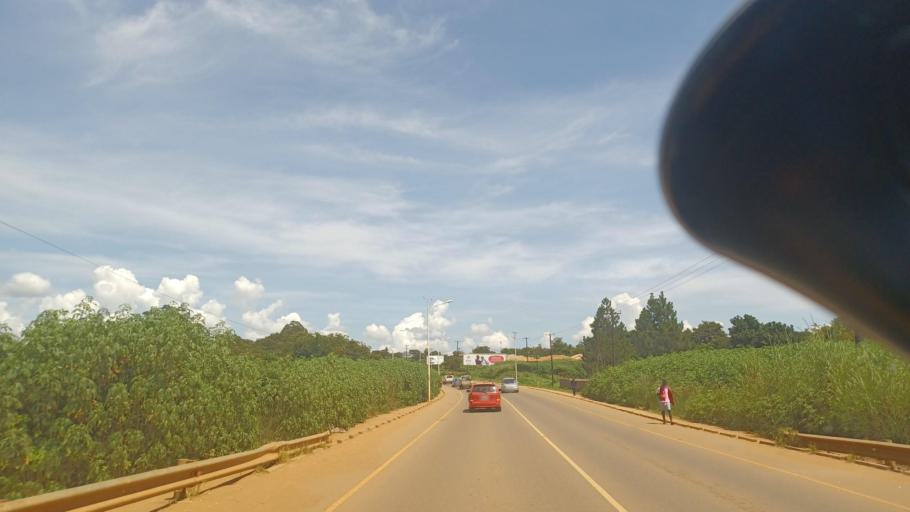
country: ZM
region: North-Western
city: Solwezi
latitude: -12.1886
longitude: 26.4319
